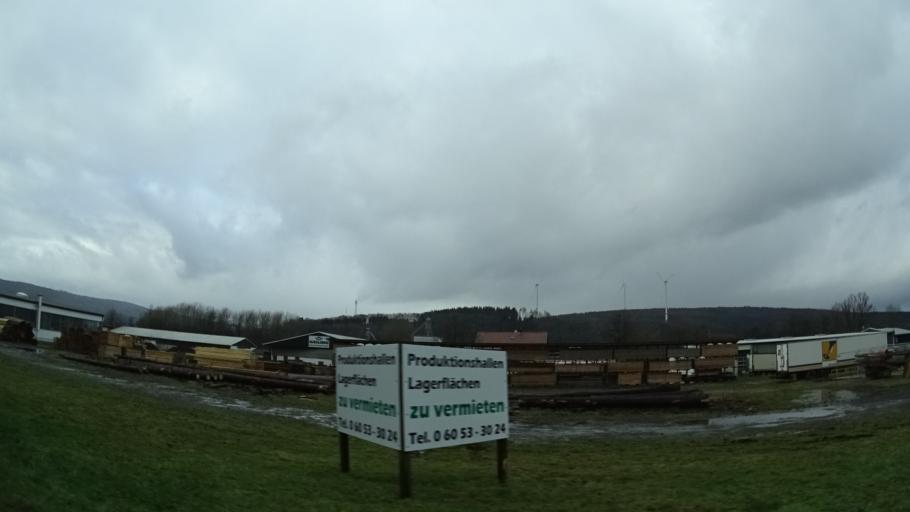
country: DE
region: Hesse
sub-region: Regierungsbezirk Darmstadt
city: Bad Orb
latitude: 50.2557
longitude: 9.3356
